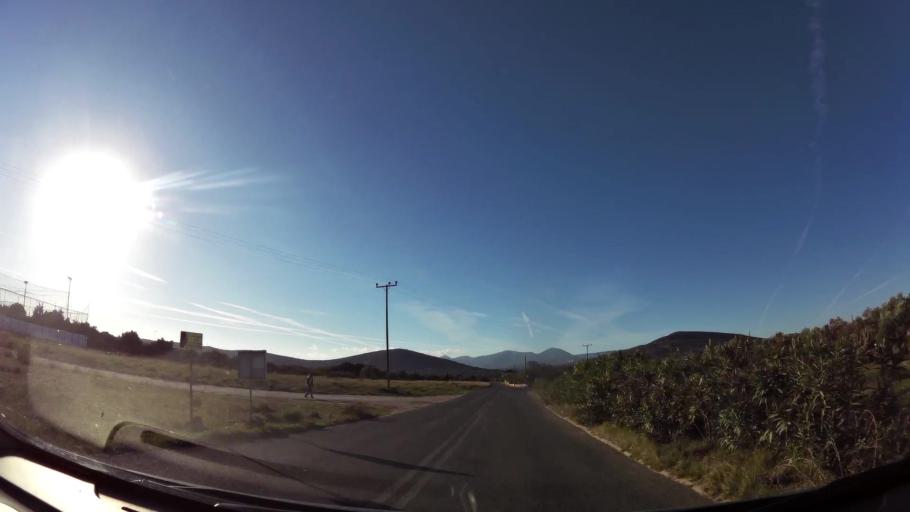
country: GR
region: Attica
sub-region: Nomarchia Anatolikis Attikis
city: Kalyvia Thorikou
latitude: 37.8449
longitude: 23.9230
